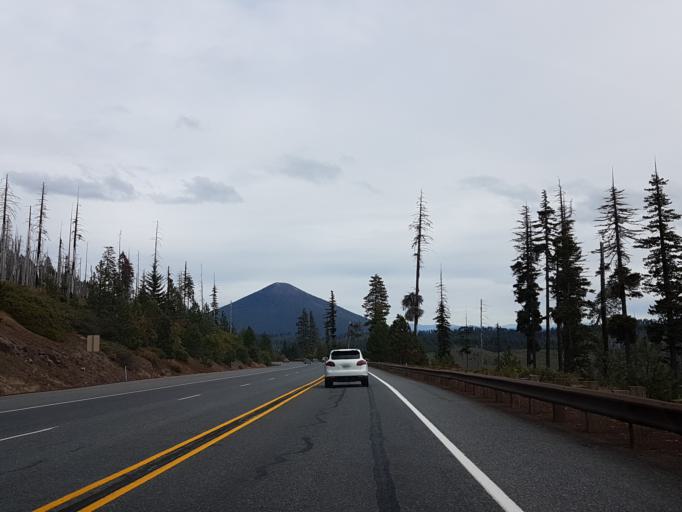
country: US
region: Oregon
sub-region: Deschutes County
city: Sisters
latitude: 44.4192
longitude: -121.7841
